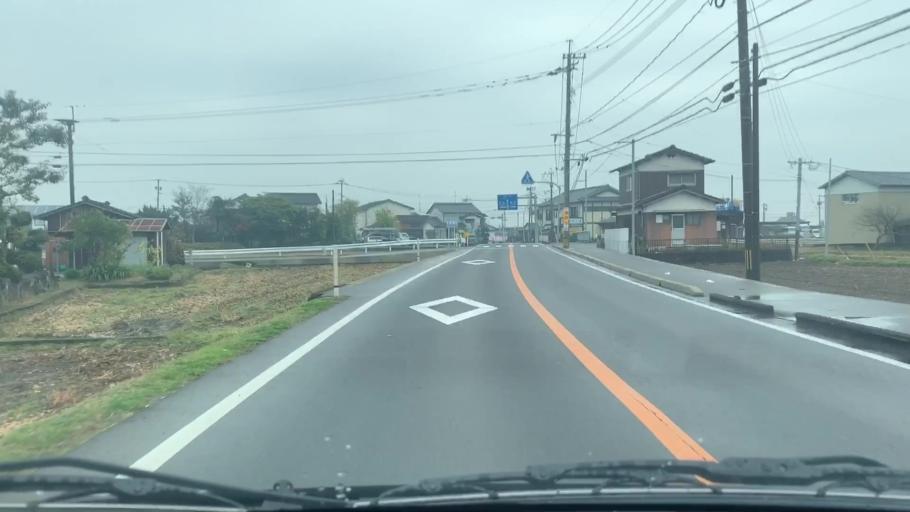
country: JP
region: Saga Prefecture
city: Takeocho-takeo
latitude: 33.1956
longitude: 130.1125
